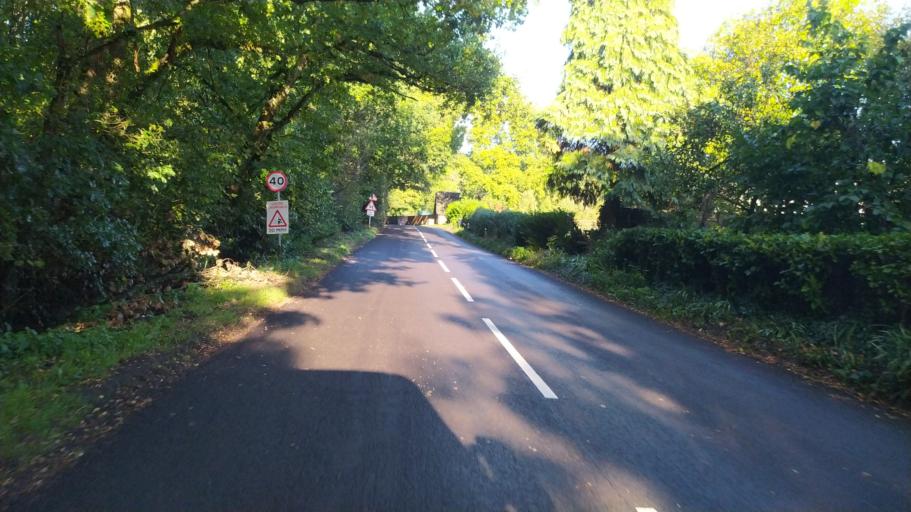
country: GB
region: England
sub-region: Dorset
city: Three Legged Cross
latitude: 50.8586
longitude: -1.9229
